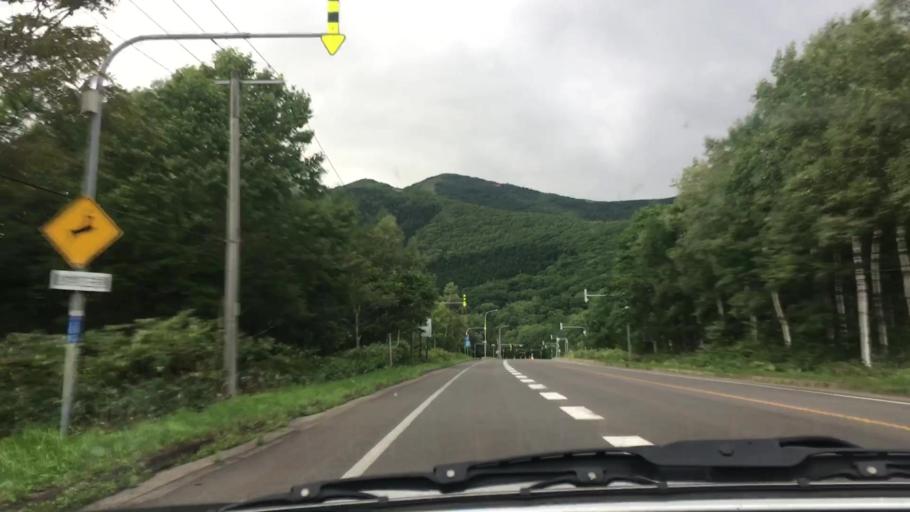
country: JP
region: Hokkaido
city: Otofuke
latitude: 43.1629
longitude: 142.8109
